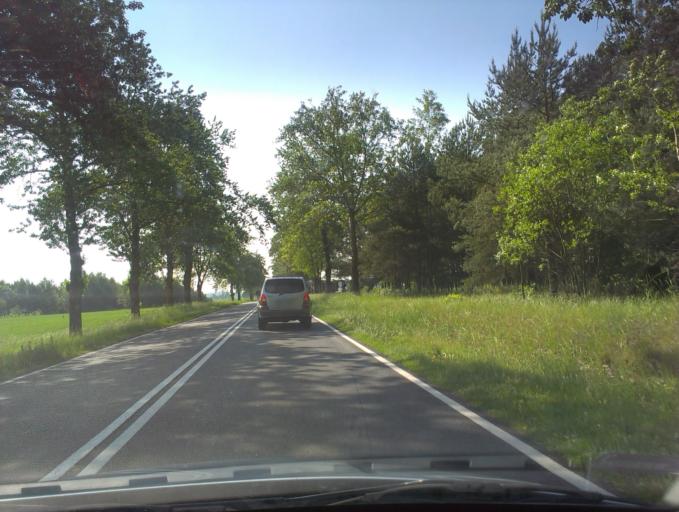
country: PL
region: Greater Poland Voivodeship
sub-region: Powiat zlotowski
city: Okonek
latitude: 53.5750
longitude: 16.8262
